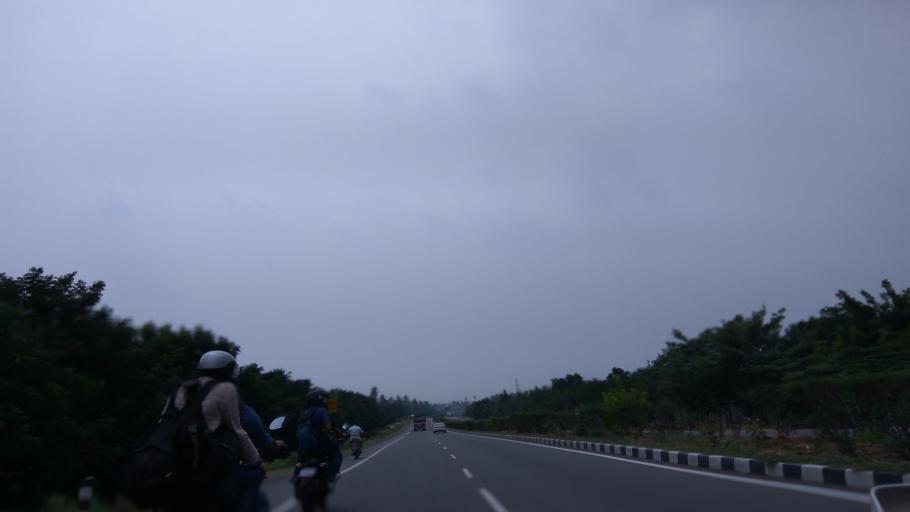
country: IN
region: Tamil Nadu
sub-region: Krishnagiri
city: Kaverippattanam
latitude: 12.3291
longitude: 78.2116
